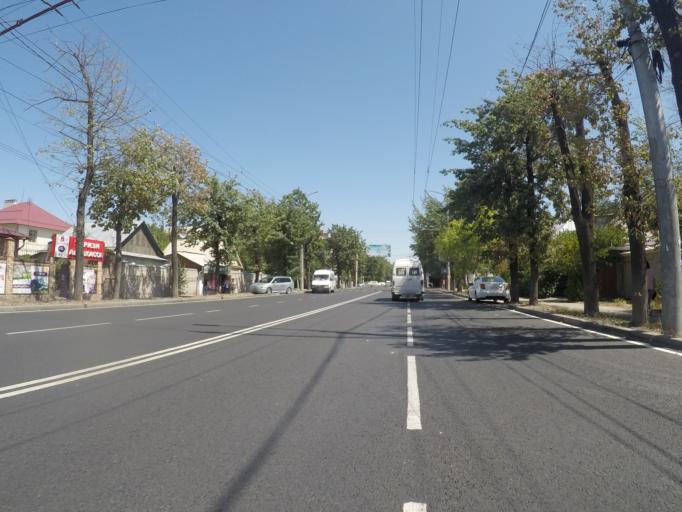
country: KG
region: Chuy
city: Bishkek
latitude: 42.8436
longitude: 74.5800
